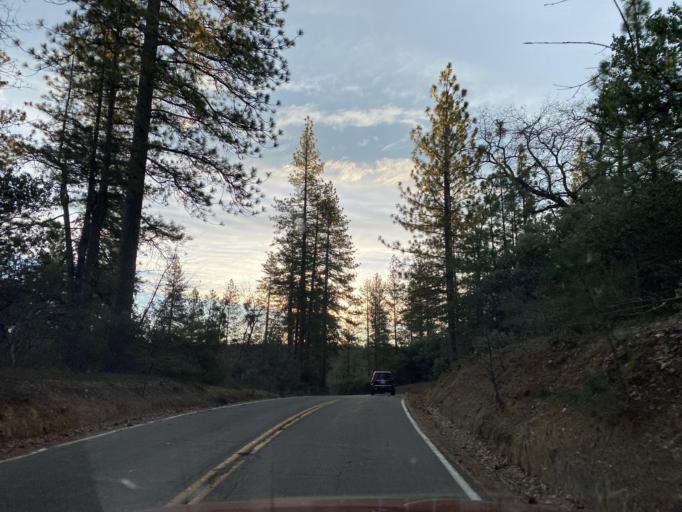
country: US
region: California
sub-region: Amador County
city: Pioneer
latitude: 38.4989
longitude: -120.6078
